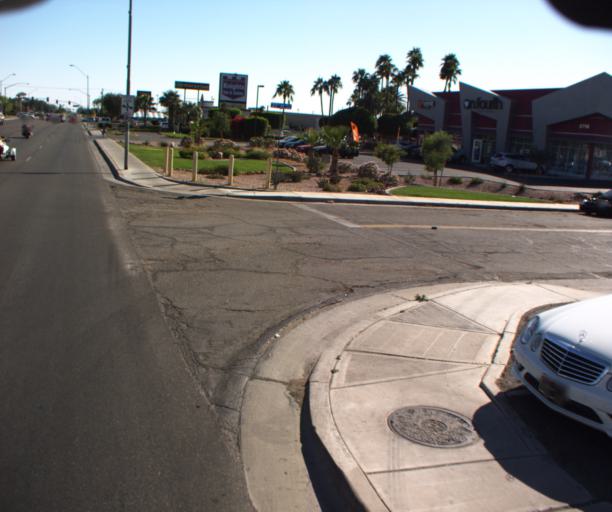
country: US
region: Arizona
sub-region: Yuma County
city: Yuma
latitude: 32.6786
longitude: -114.6246
